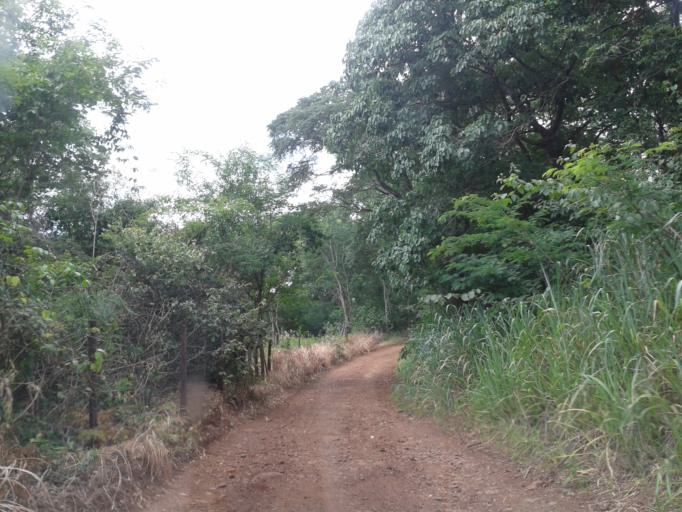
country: BR
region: Minas Gerais
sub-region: Centralina
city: Centralina
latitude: -18.6838
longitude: -49.2240
